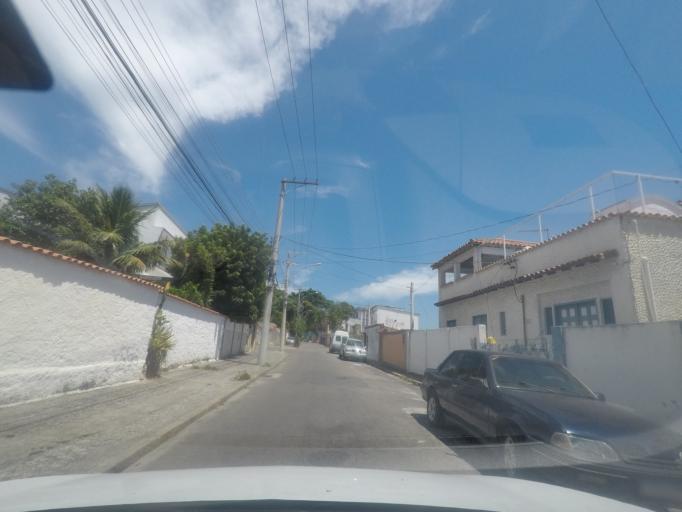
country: BR
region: Rio de Janeiro
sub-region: Itaguai
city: Itaguai
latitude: -23.0046
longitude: -43.6395
